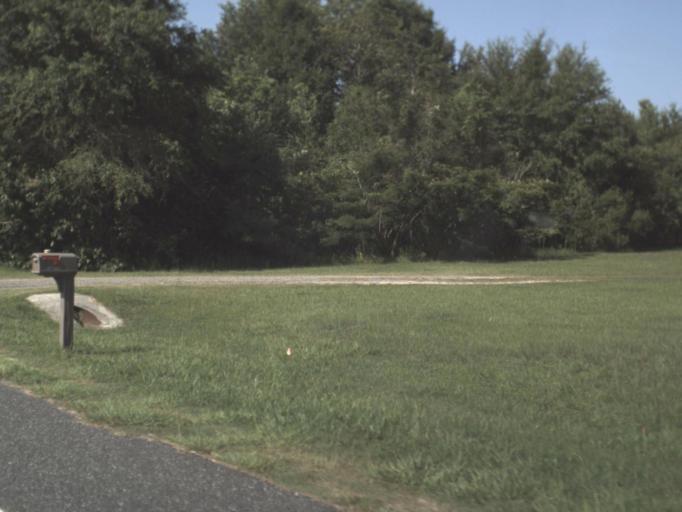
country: US
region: Florida
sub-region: Columbia County
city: Lake City
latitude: 30.0034
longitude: -82.7102
